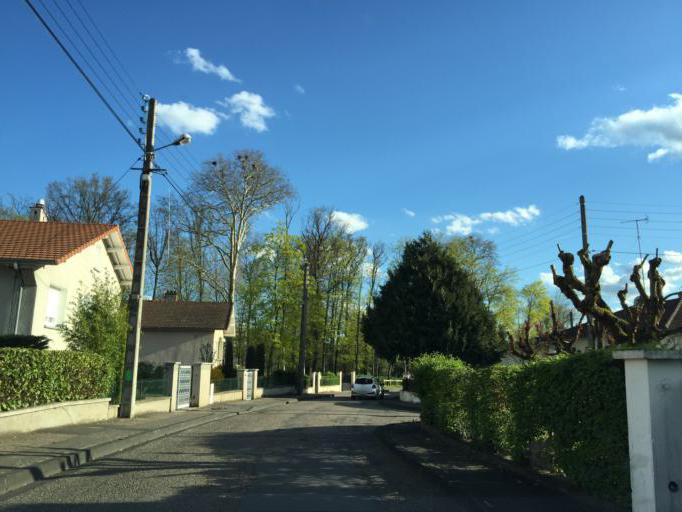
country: FR
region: Rhone-Alpes
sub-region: Departement de la Loire
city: Feurs
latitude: 45.7502
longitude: 4.2229
